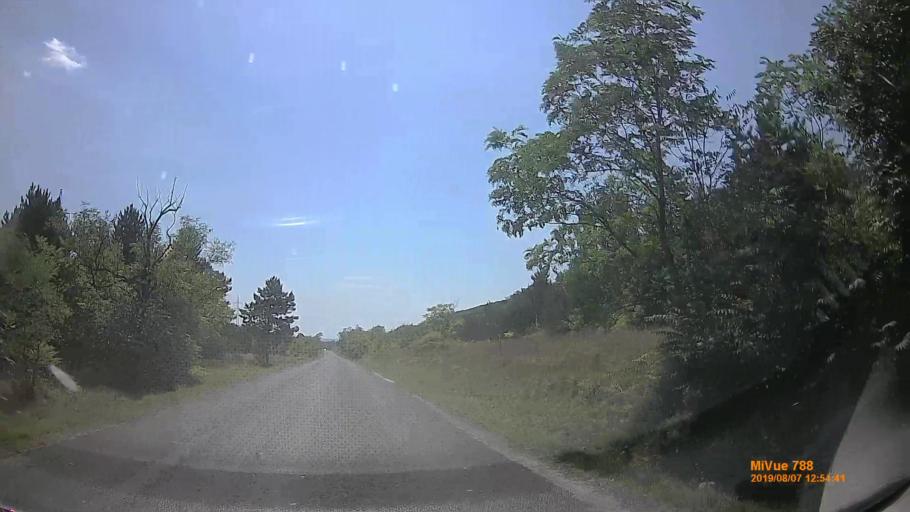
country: HU
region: Zala
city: Gyenesdias
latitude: 46.8204
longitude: 17.2706
